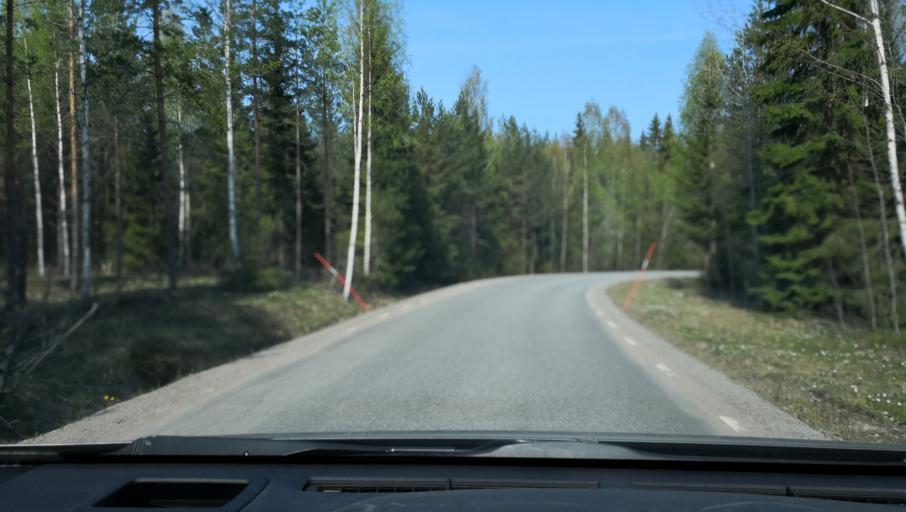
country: SE
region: Vaestmanland
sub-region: Sala Kommun
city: Sala
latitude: 59.9990
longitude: 16.6592
